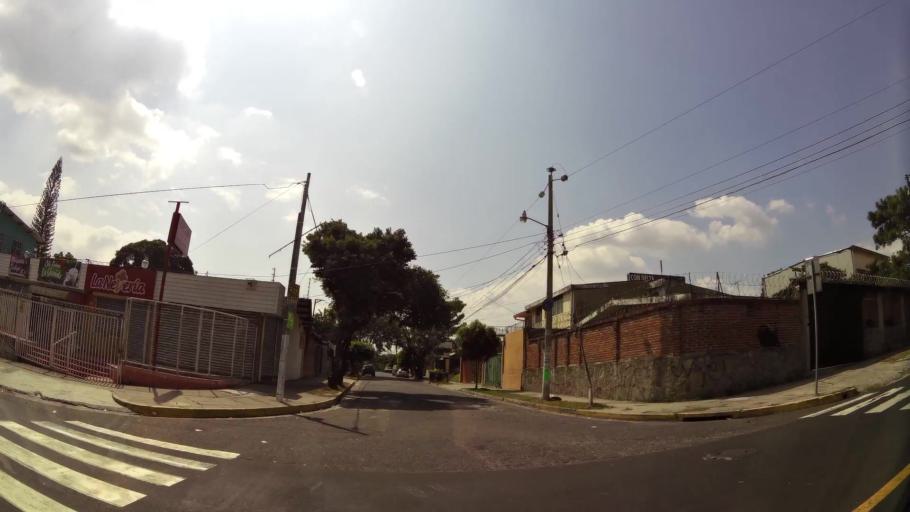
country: SV
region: San Salvador
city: Mejicanos
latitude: 13.7124
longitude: -89.2171
